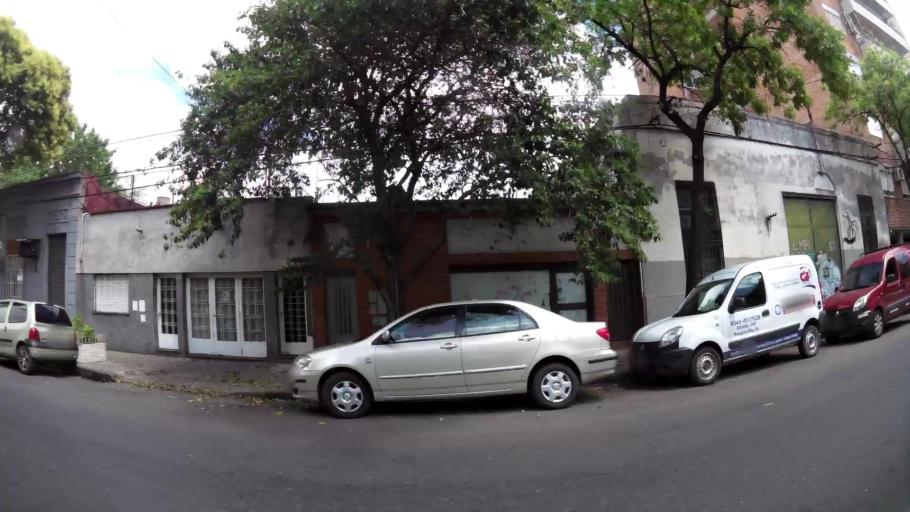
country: AR
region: Santa Fe
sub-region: Departamento de Rosario
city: Rosario
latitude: -32.9667
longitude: -60.6330
